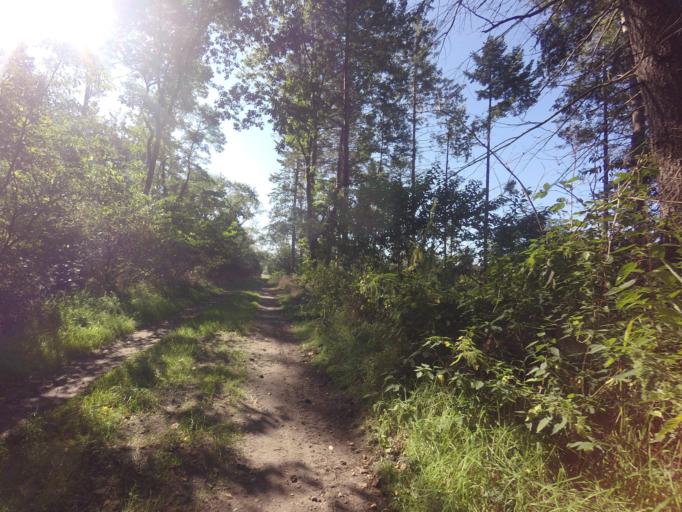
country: DE
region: Lower Saxony
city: Wielen
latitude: 52.5397
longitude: 6.7172
